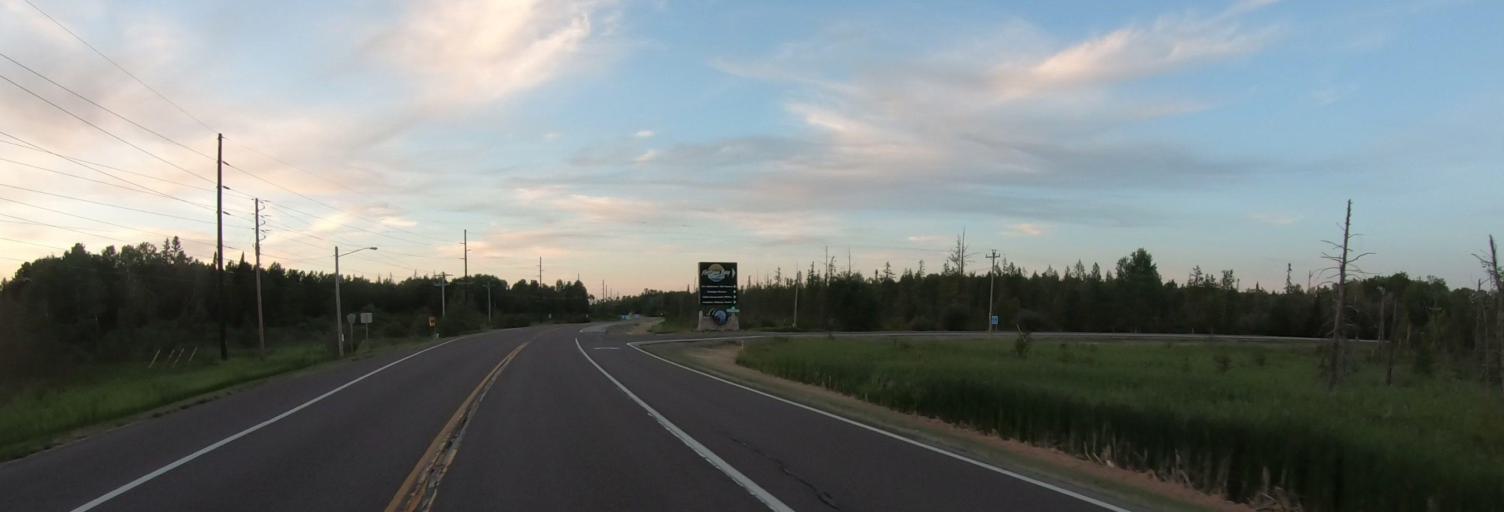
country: US
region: Minnesota
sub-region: Saint Louis County
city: Aurora
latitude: 47.8088
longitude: -92.3725
